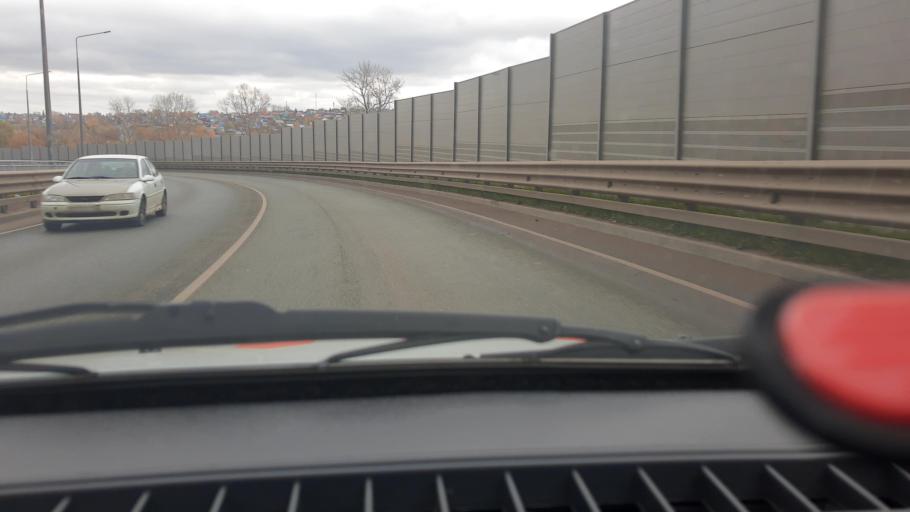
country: RU
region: Bashkortostan
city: Ufa
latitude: 54.8281
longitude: 56.1282
